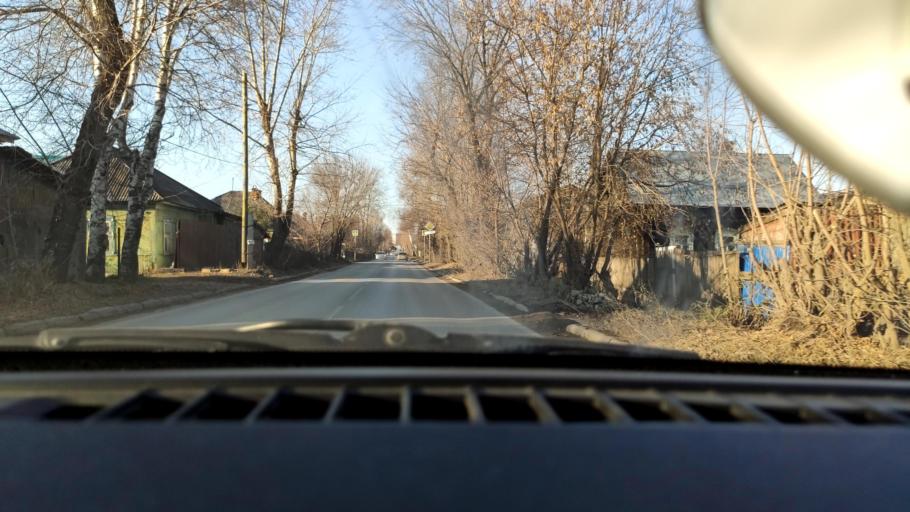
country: RU
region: Perm
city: Perm
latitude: 58.0131
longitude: 56.3197
